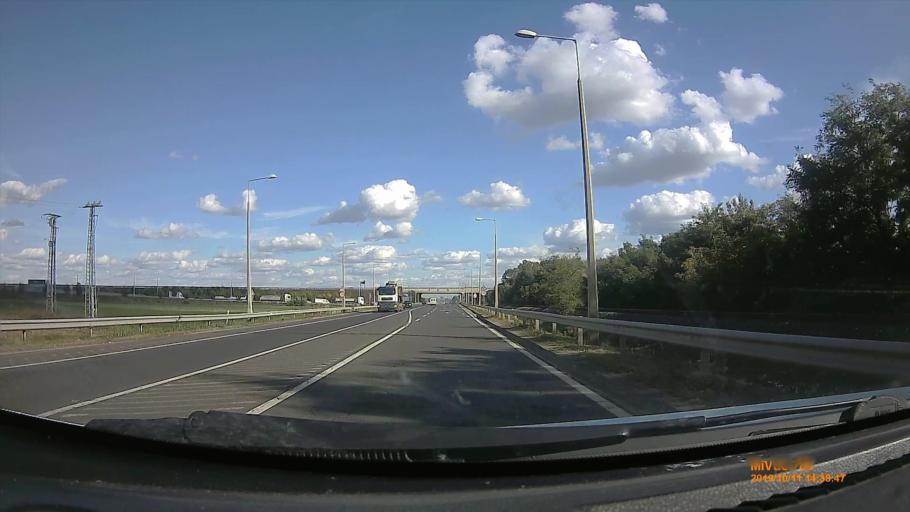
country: HU
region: Hajdu-Bihar
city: Debrecen
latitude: 47.5502
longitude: 21.5468
